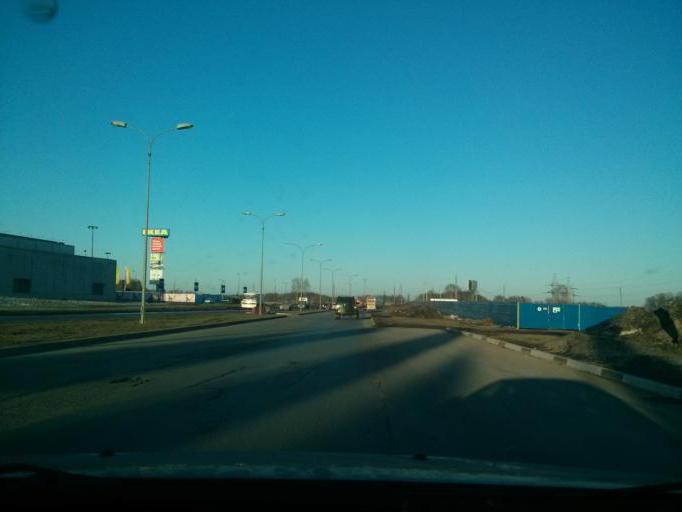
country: RU
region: Nizjnij Novgorod
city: Afonino
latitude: 56.2223
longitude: 44.0725
